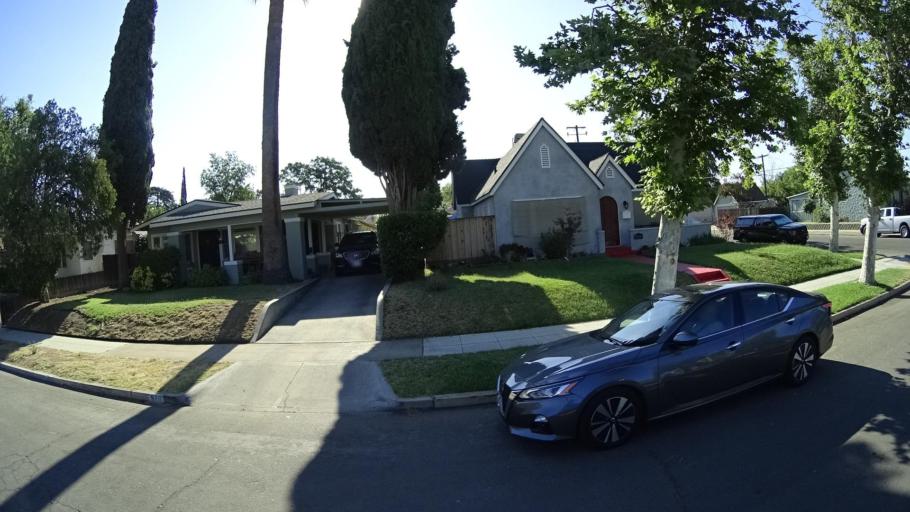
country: US
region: California
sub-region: Fresno County
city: Fresno
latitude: 36.7542
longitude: -119.8143
